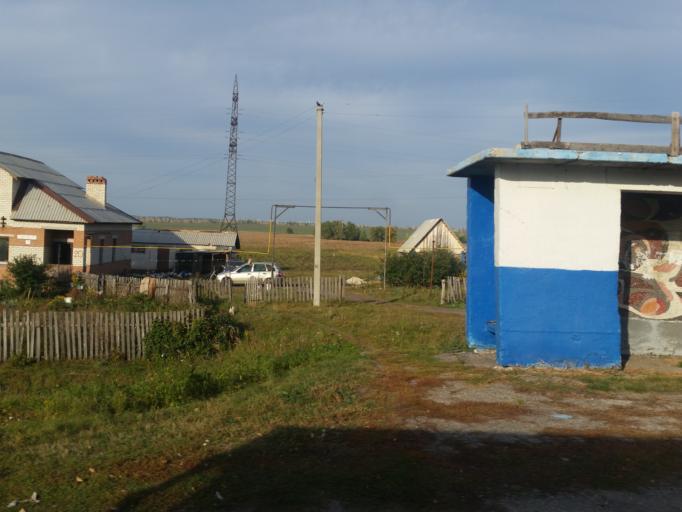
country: RU
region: Ulyanovsk
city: Mullovka
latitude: 54.2671
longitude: 49.1669
